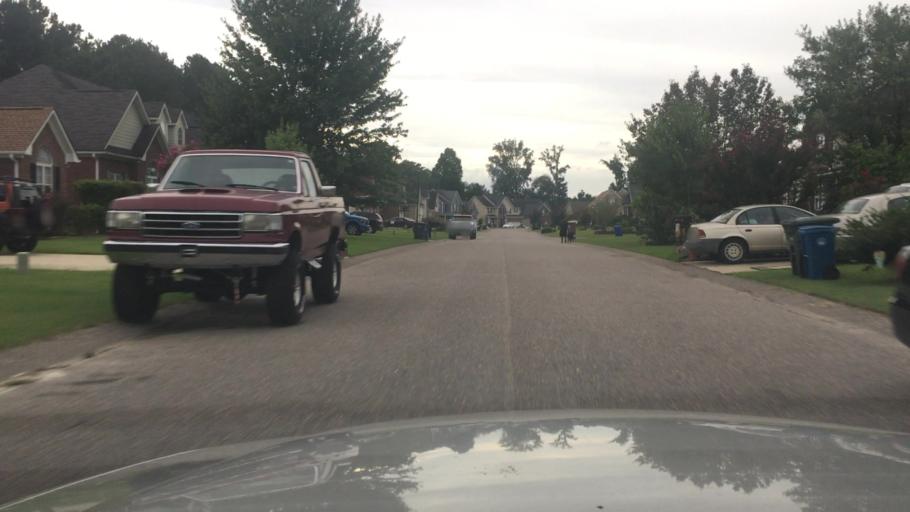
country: US
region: North Carolina
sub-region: Hoke County
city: Rockfish
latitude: 34.9947
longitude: -79.0265
